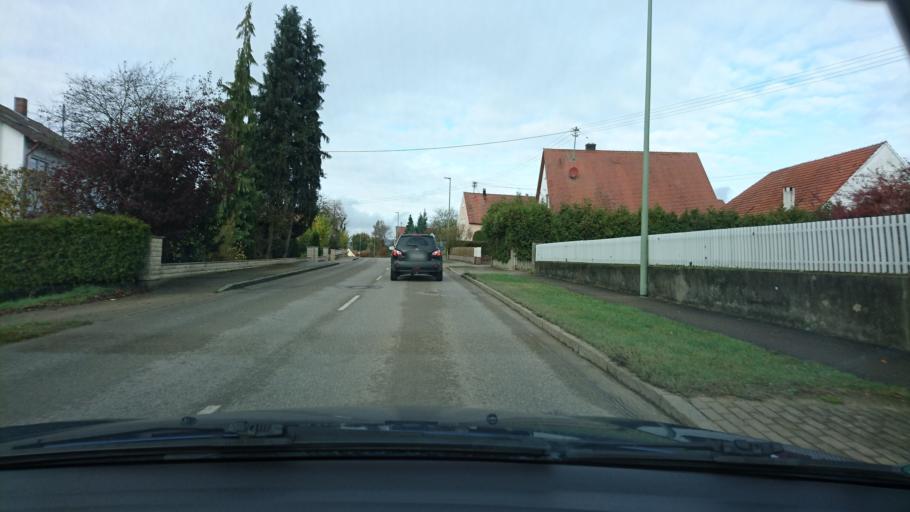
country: DE
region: Bavaria
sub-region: Swabia
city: Tapfheim
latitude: 48.6970
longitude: 10.6780
